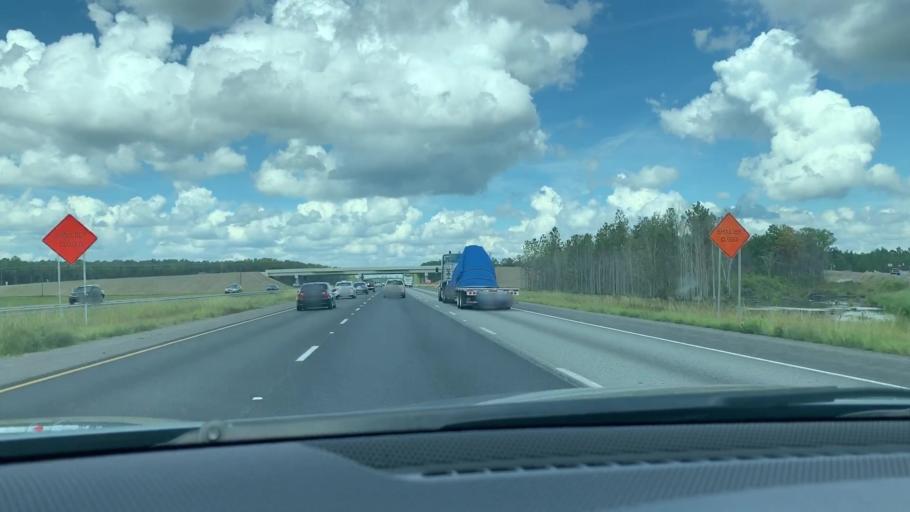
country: US
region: Georgia
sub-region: Camden County
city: Kingsland
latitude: 30.8225
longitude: -81.6658
